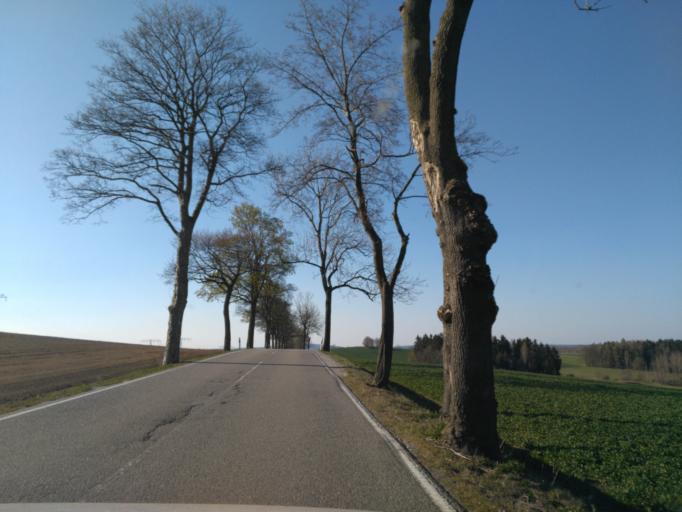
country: DE
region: Saxony
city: Scheibenberg
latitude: 50.5179
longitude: 12.9151
